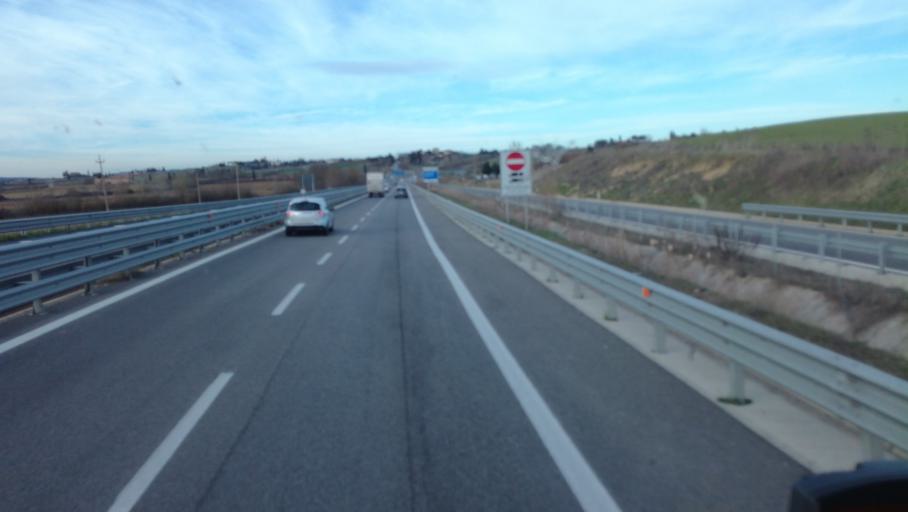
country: IT
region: Tuscany
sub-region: Provincia di Siena
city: Rosia
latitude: 43.2342
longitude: 11.2775
